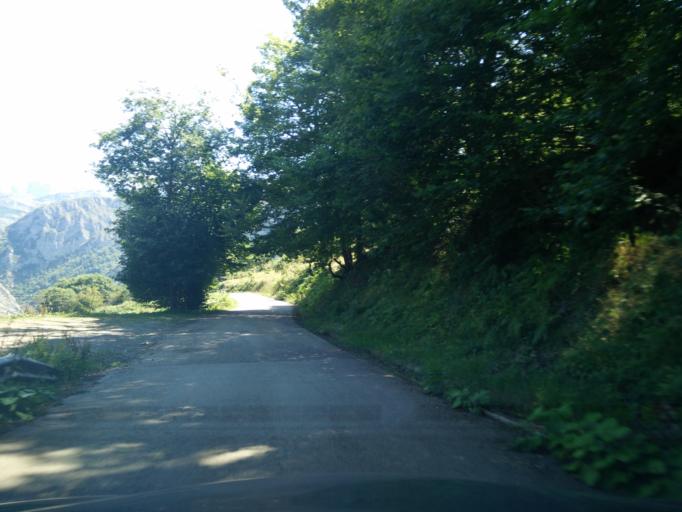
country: ES
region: Asturias
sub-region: Province of Asturias
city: Amieva
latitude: 43.1947
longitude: -5.1333
